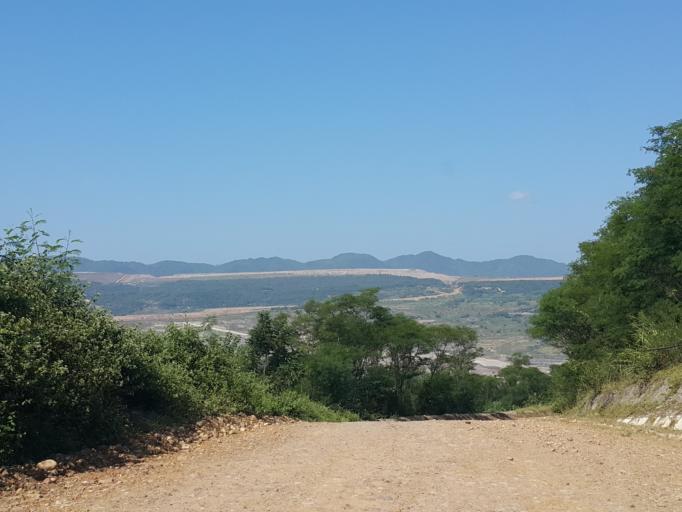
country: TH
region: Lampang
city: Mae Mo
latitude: 18.3238
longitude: 99.7405
